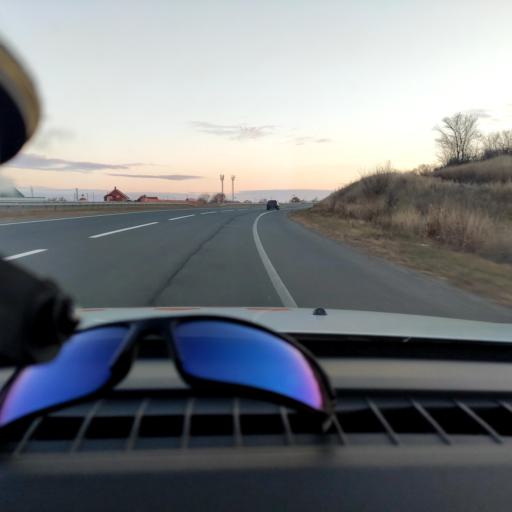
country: RU
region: Samara
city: Novokuybyshevsk
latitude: 53.0618
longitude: 50.0200
